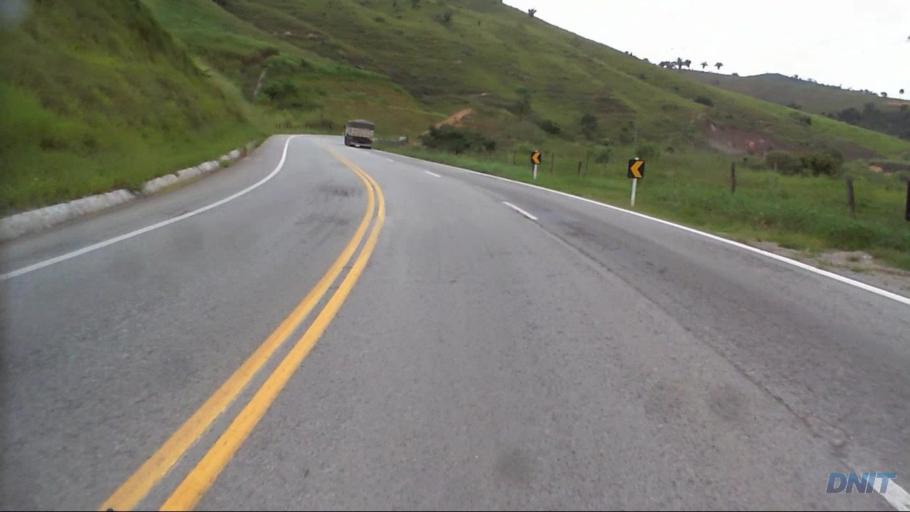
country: BR
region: Minas Gerais
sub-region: Nova Era
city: Nova Era
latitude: -19.6487
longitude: -42.9331
